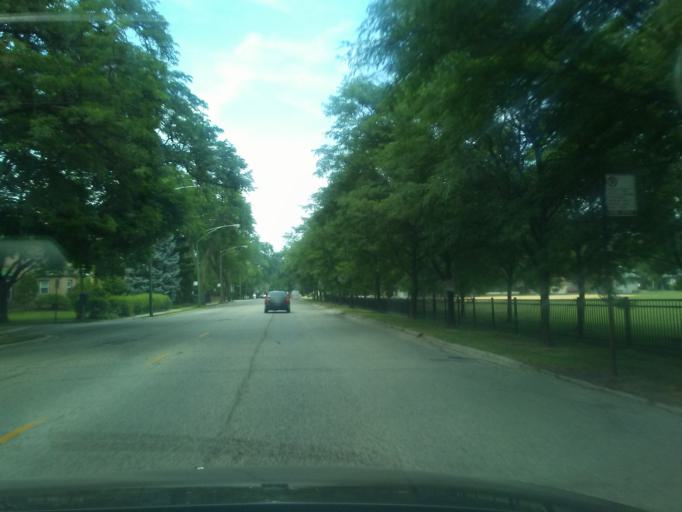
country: US
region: Illinois
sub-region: Cook County
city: Lincolnwood
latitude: 42.0005
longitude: -87.7627
